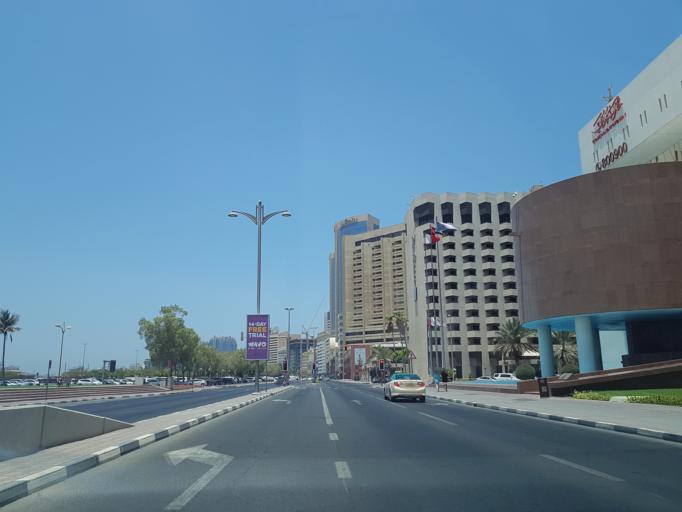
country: AE
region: Ash Shariqah
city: Sharjah
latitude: 25.2639
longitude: 55.3116
